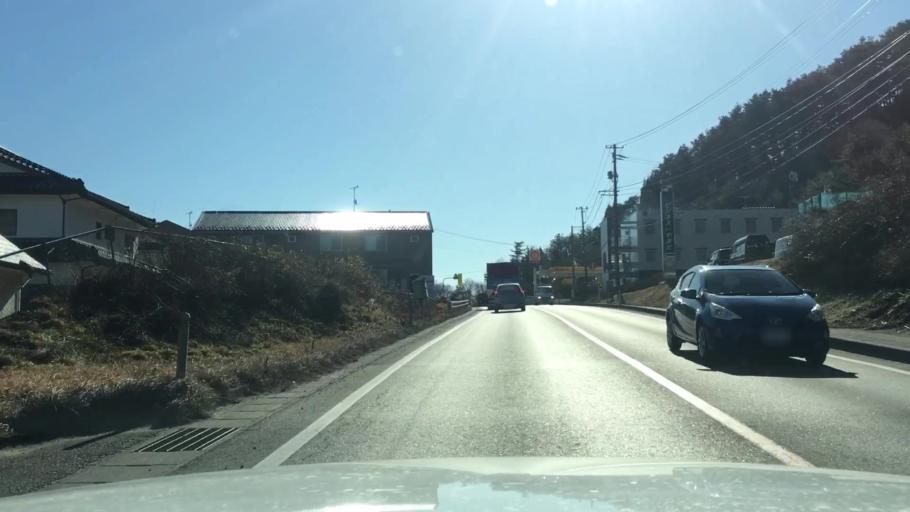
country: JP
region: Iwate
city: Yamada
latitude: 39.4453
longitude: 141.9700
